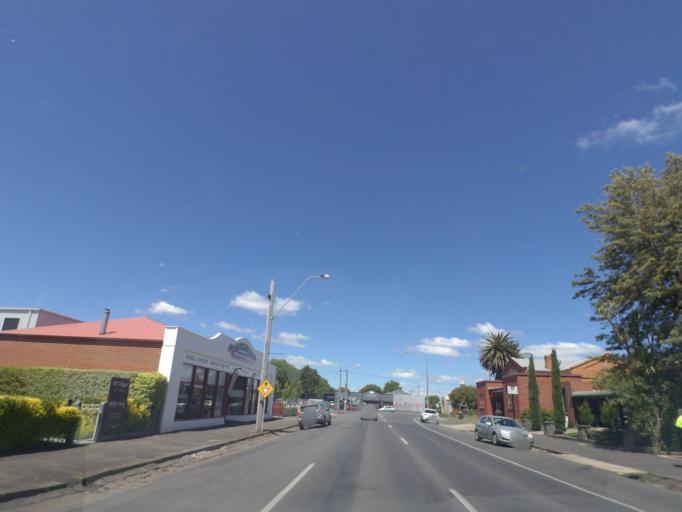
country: AU
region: Victoria
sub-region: Mount Alexander
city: Castlemaine
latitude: -37.2446
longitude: 144.4531
